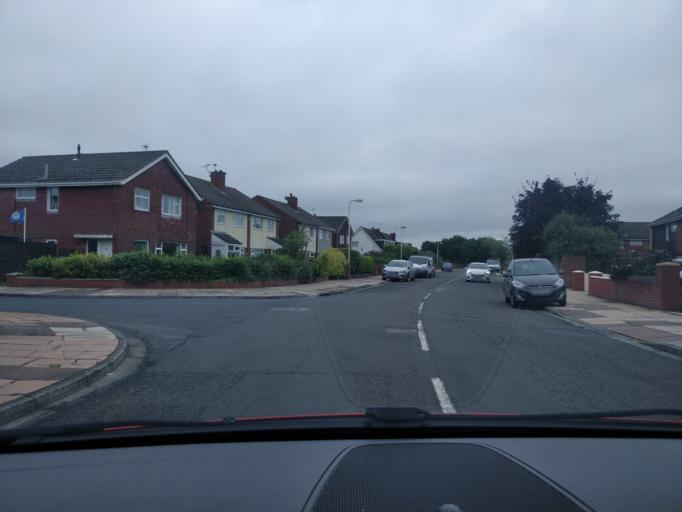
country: GB
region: England
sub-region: Lancashire
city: Banks
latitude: 53.6760
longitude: -2.9595
